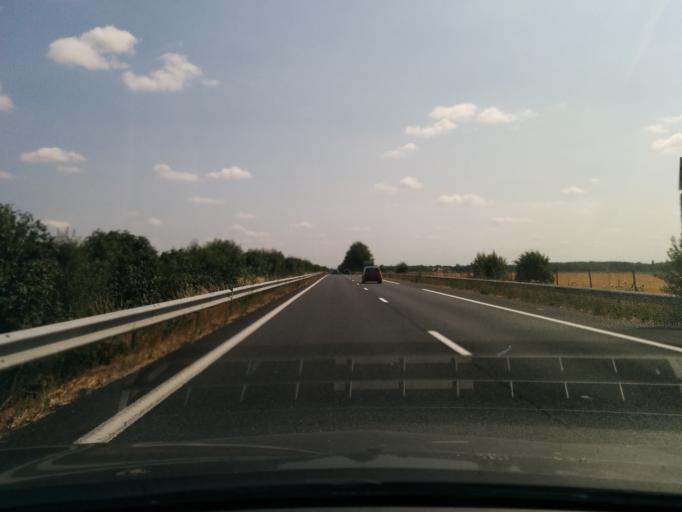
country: FR
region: Centre
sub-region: Departement de l'Indre
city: Montierchaume
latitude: 46.9442
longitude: 1.7523
